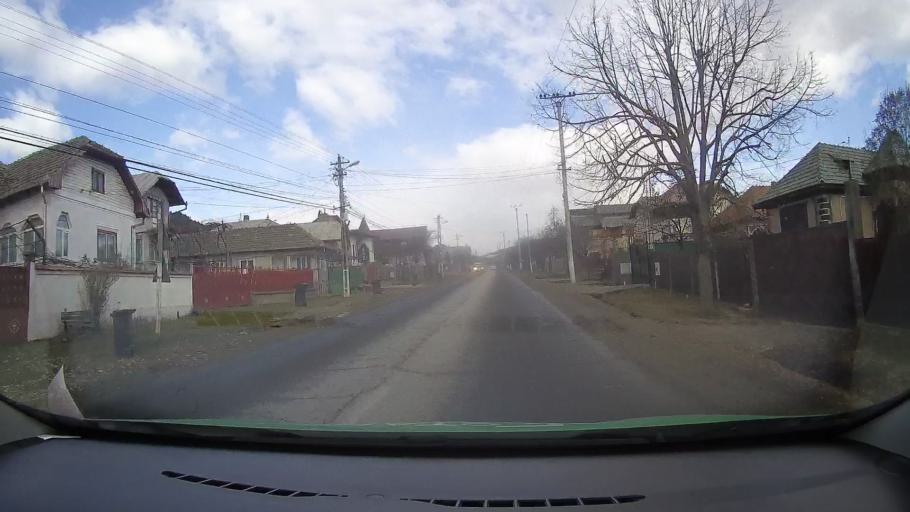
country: RO
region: Dambovita
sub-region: Comuna Buciumeni
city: Buciumeni
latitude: 45.1521
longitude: 25.4464
